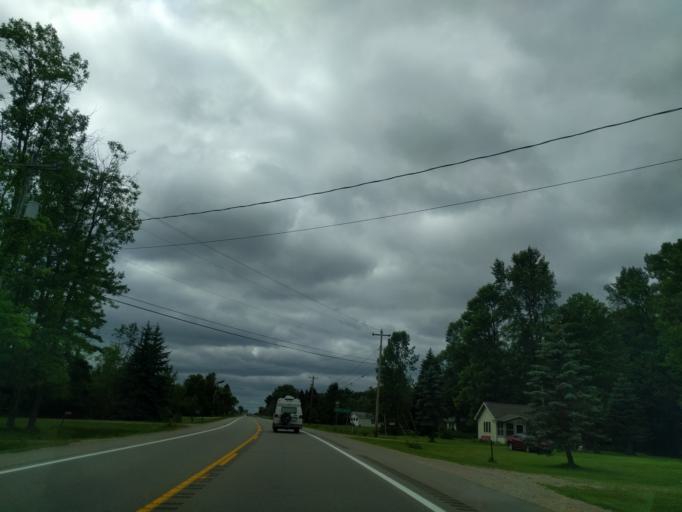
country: US
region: Michigan
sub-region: Menominee County
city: Menominee
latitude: 45.2043
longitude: -87.5363
